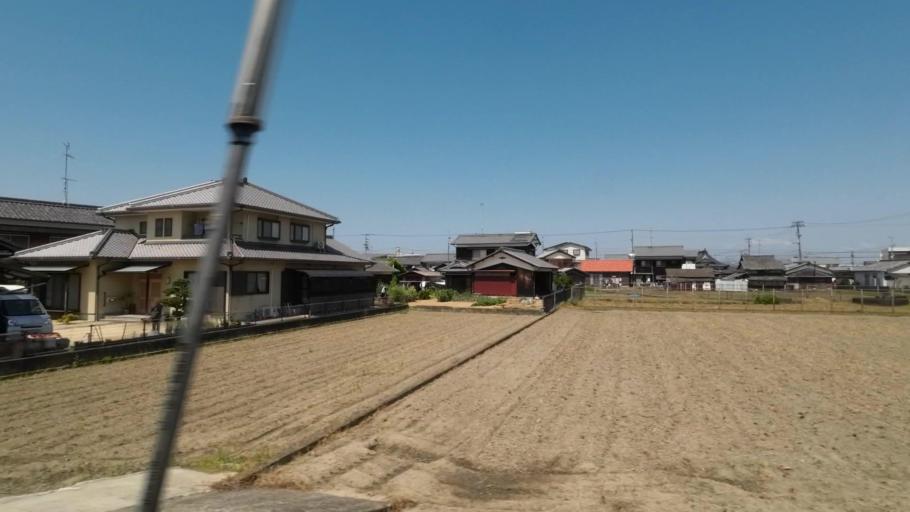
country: JP
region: Ehime
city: Hojo
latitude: 34.0361
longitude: 132.8454
